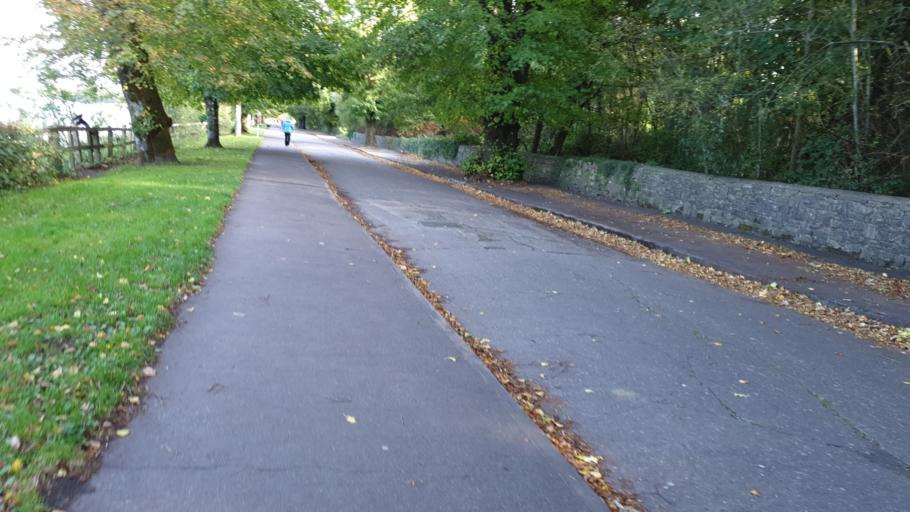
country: IE
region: Munster
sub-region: County Cork
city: Cork
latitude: 51.8998
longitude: -8.4264
